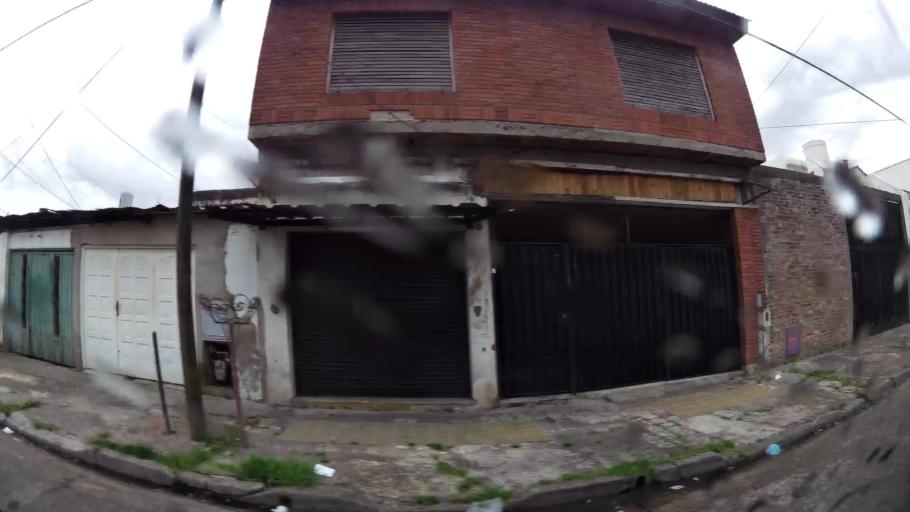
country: AR
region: Buenos Aires
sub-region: Partido de Lanus
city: Lanus
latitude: -34.6846
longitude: -58.4027
